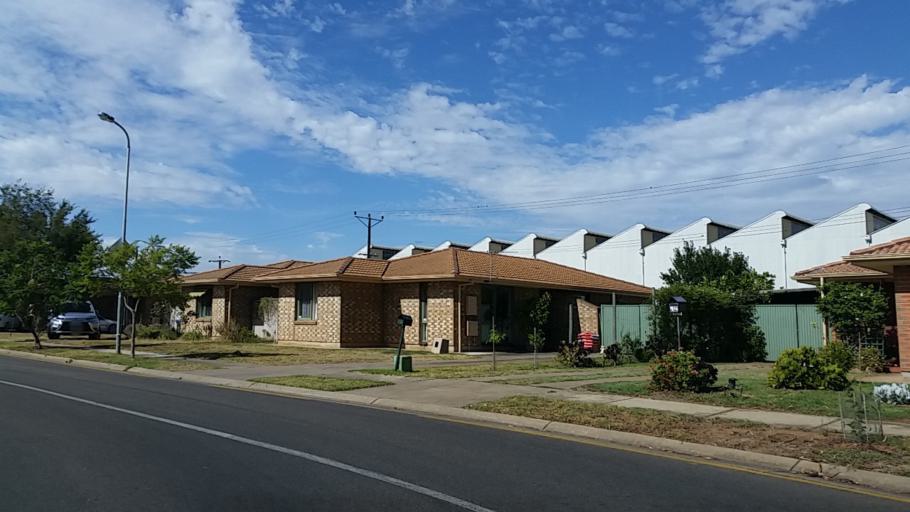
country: AU
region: South Australia
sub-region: Port Adelaide Enfield
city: Alberton
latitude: -34.8543
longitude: 138.5362
